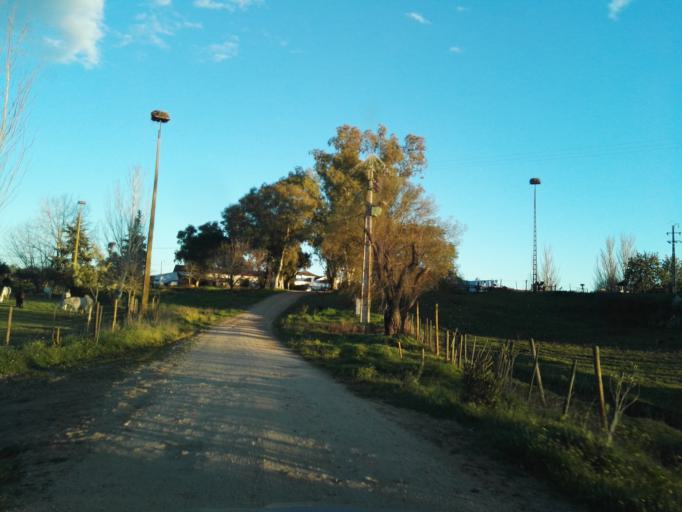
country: PT
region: Castelo Branco
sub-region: Idanha-A-Nova
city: Idanha-a-Nova
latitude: 39.8636
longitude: -7.1349
